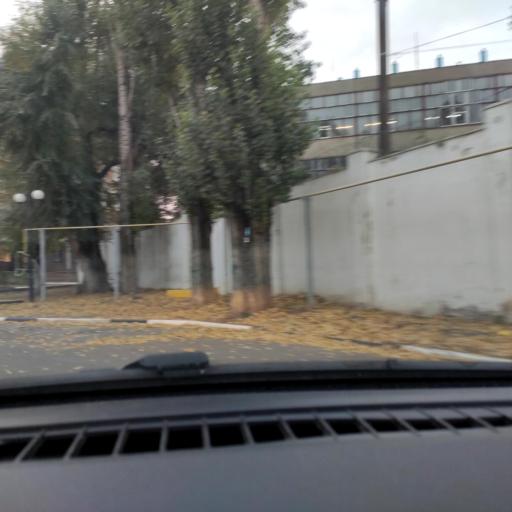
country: RU
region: Voronezj
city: Voronezh
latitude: 51.6618
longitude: 39.1511
